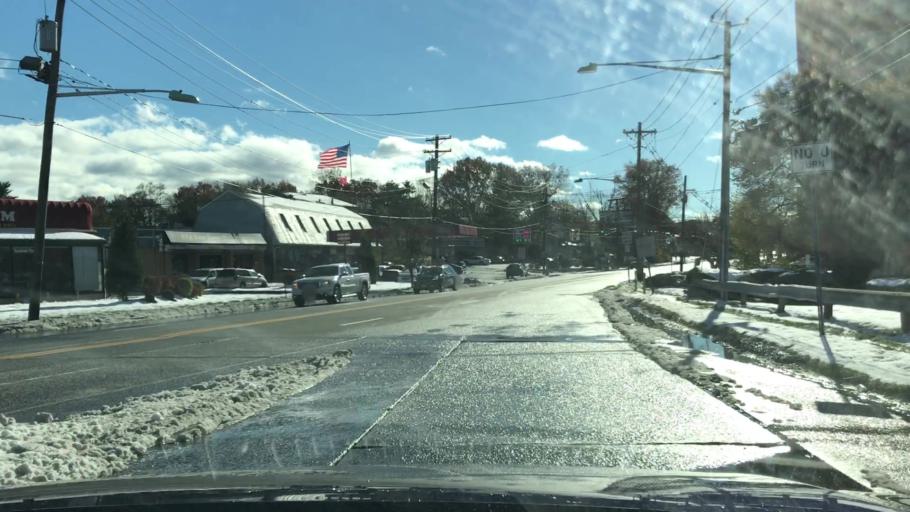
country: US
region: New Jersey
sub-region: Bergen County
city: Lodi
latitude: 40.8762
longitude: -74.0652
